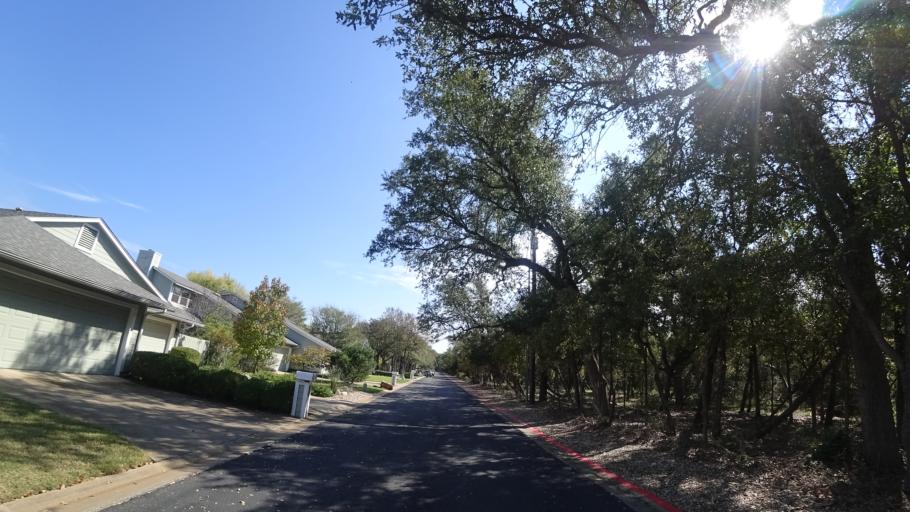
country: US
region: Texas
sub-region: Travis County
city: Shady Hollow
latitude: 30.2119
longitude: -97.8278
